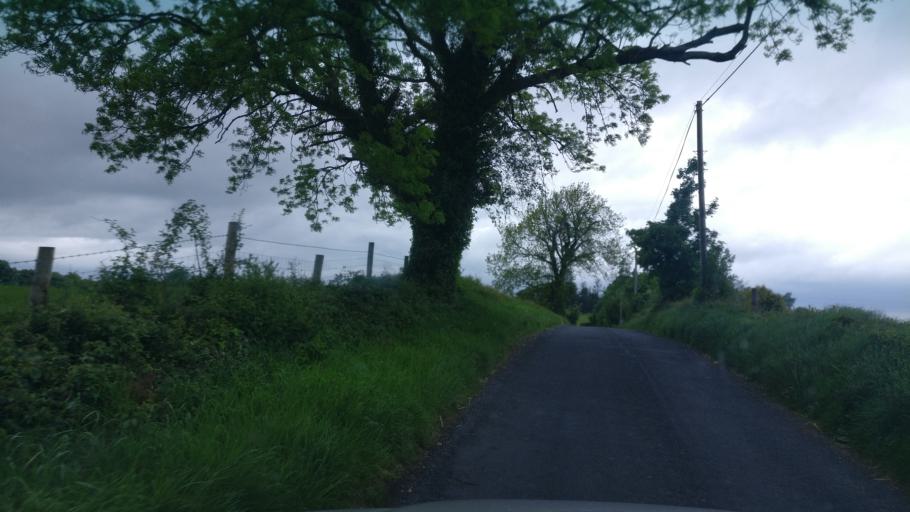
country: IE
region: Connaught
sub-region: County Galway
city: Portumna
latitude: 53.1482
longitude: -8.2910
